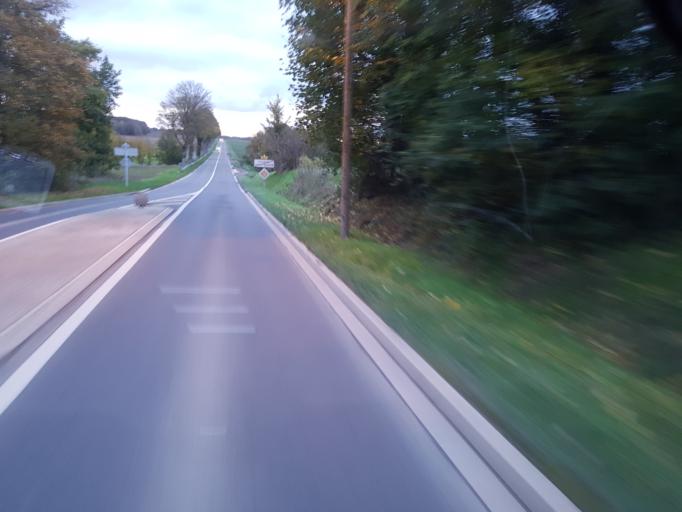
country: FR
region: Picardie
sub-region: Departement de l'Aisne
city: Coincy
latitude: 49.1549
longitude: 3.3867
